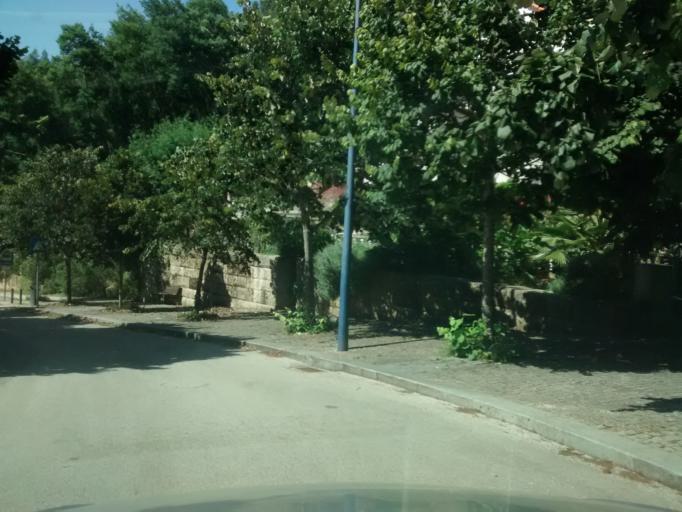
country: PT
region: Aveiro
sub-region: Mealhada
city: Pampilhosa do Botao
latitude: 40.3820
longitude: -8.3740
